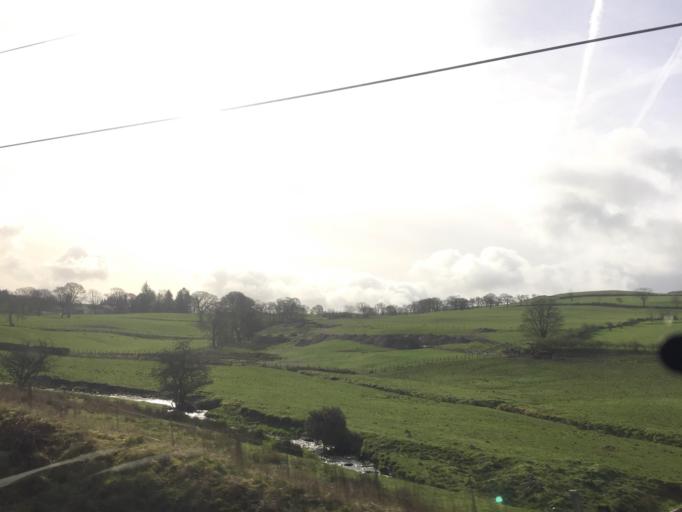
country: GB
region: England
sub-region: Cumbria
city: Sedbergh
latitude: 54.3574
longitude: -2.6299
